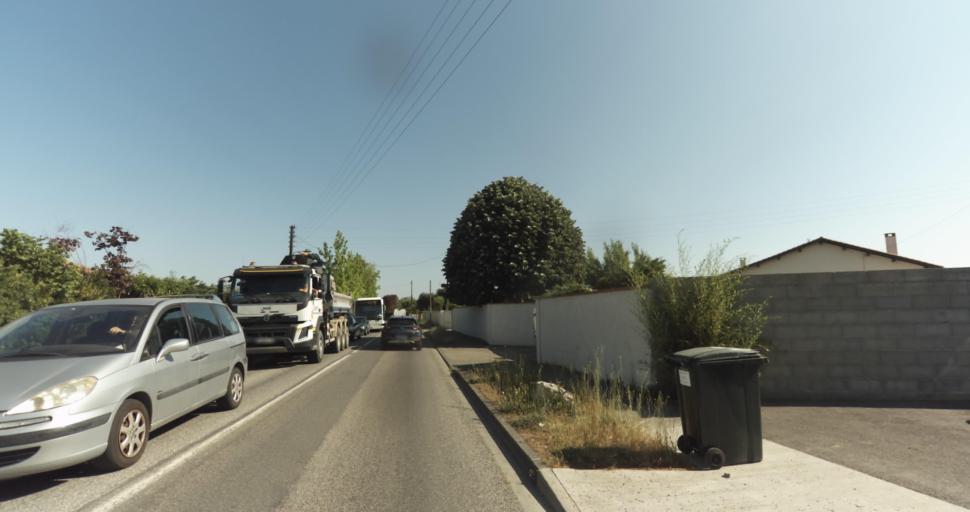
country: FR
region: Midi-Pyrenees
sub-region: Departement de la Haute-Garonne
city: Plaisance-du-Touch
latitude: 43.5773
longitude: 1.2909
